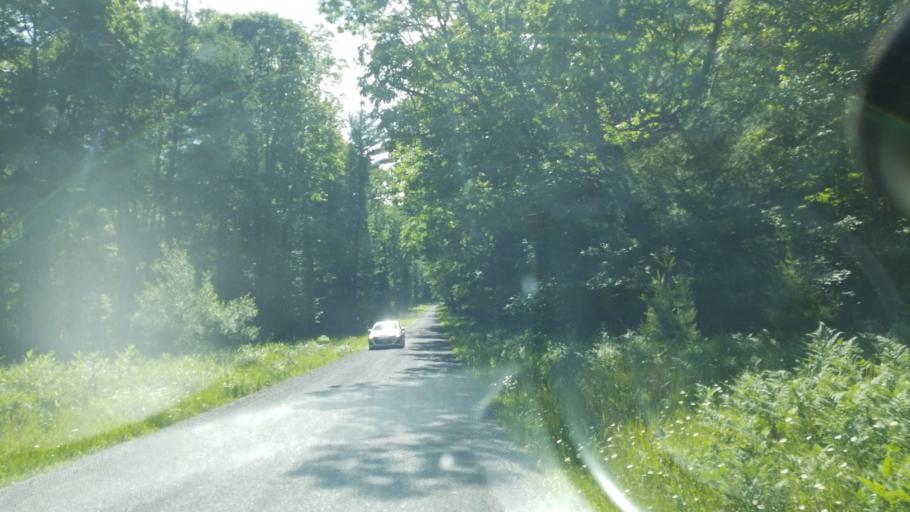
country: US
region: Pennsylvania
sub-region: Clearfield County
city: Clearfield
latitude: 41.1821
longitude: -78.4452
